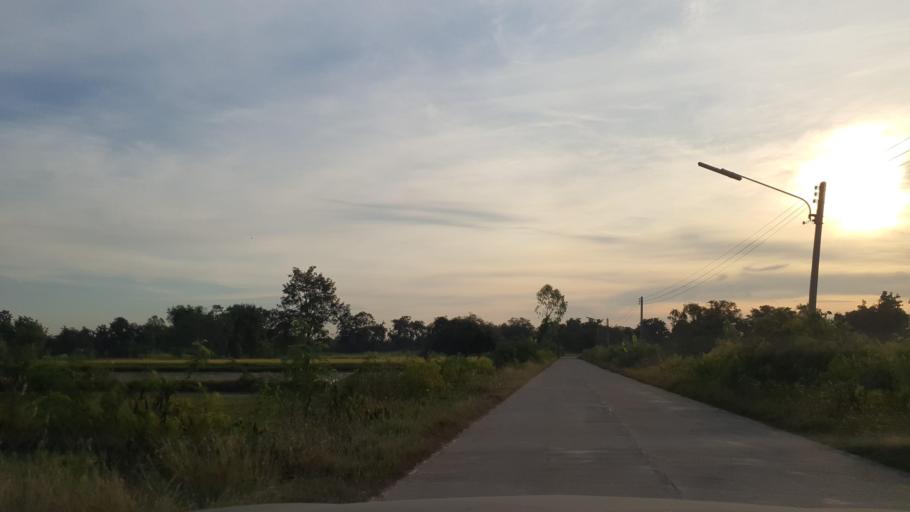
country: TH
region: Nakhon Sawan
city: Krok Phra
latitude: 15.6630
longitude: 100.0123
